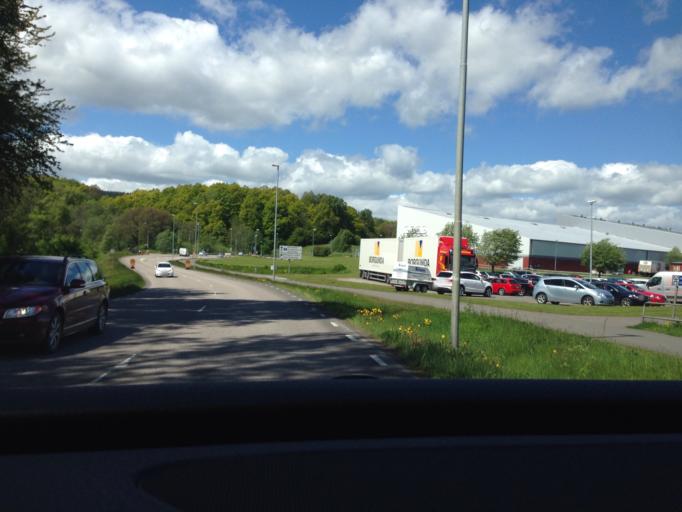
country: SE
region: Vaestra Goetaland
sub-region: Skovde Kommun
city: Skoevde
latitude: 58.4113
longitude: 13.8490
